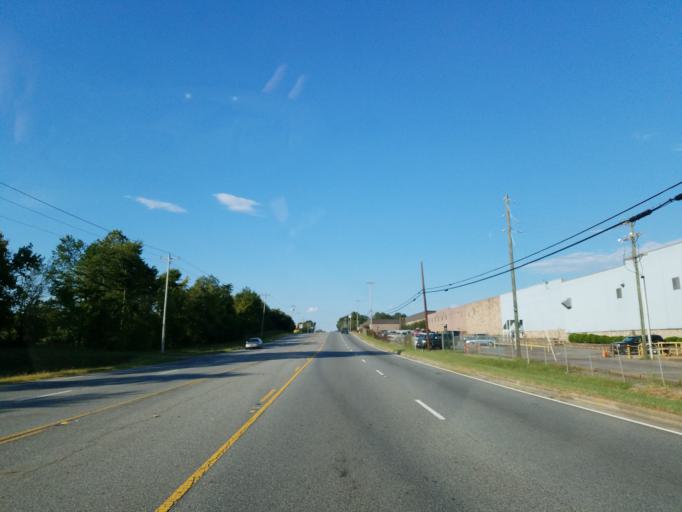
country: US
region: Georgia
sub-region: Murray County
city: Chatsworth
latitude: 34.8318
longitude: -84.7608
